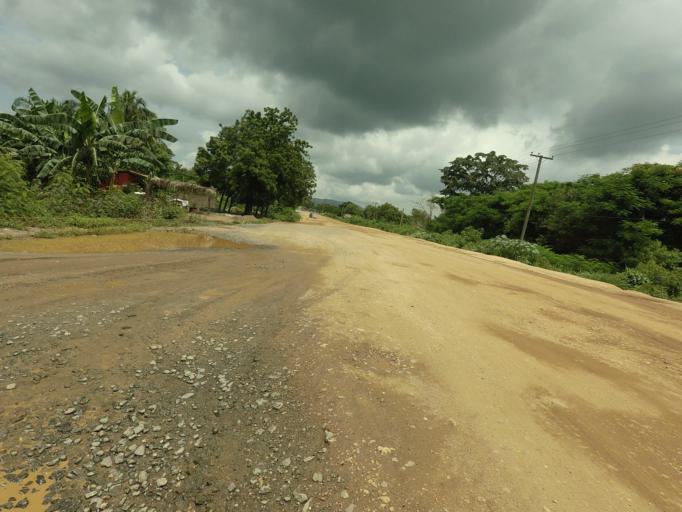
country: GH
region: Volta
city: Ho
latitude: 6.6449
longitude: 0.2984
